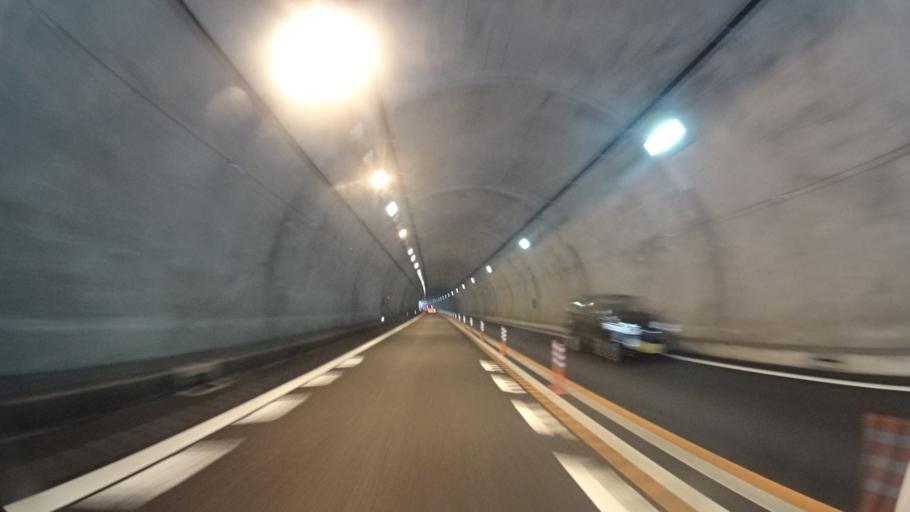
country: JP
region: Shimane
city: Izumo
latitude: 35.3258
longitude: 132.7418
